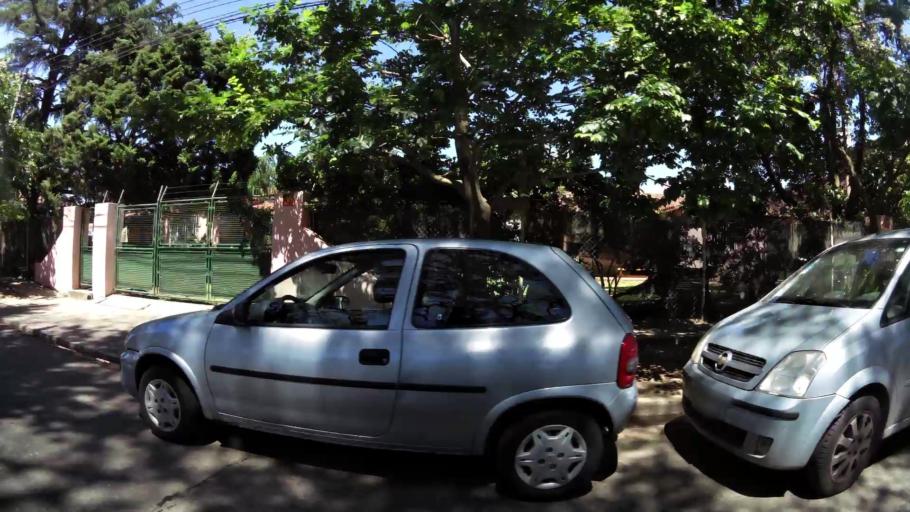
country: AR
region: Buenos Aires
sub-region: Partido de San Isidro
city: San Isidro
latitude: -34.5077
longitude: -58.5405
